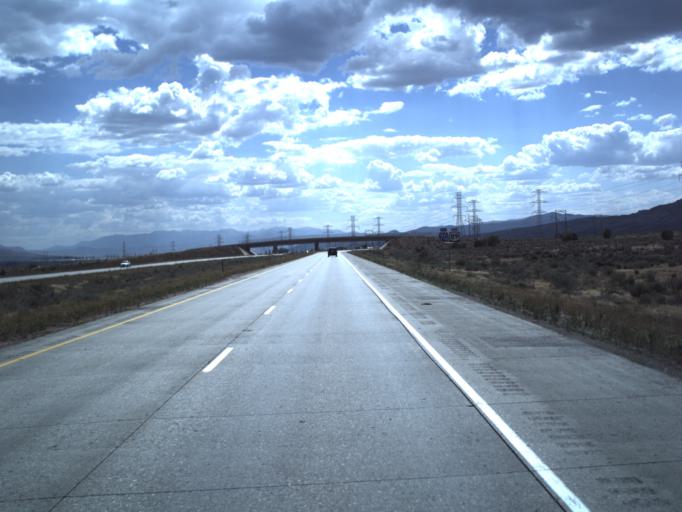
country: US
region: Utah
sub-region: Sevier County
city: Aurora
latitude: 38.8641
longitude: -111.9803
